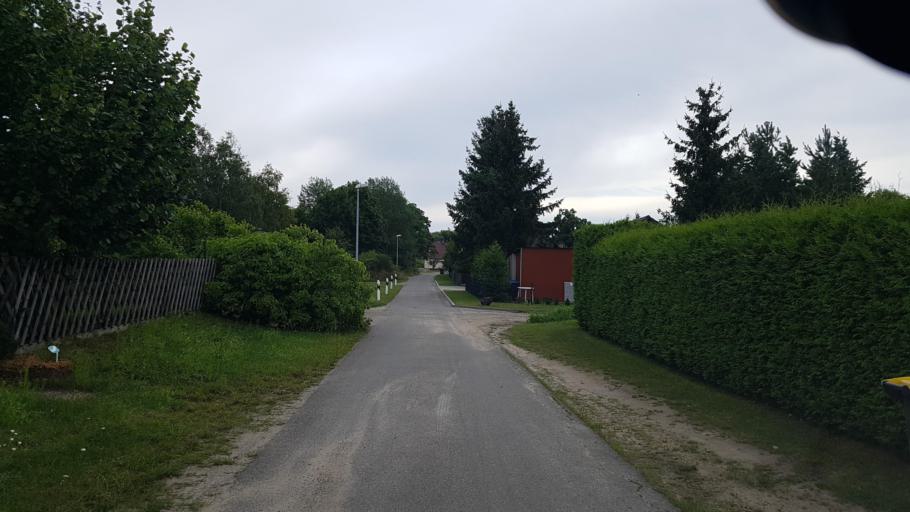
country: DE
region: Brandenburg
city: Drebkau
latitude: 51.6605
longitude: 14.1992
